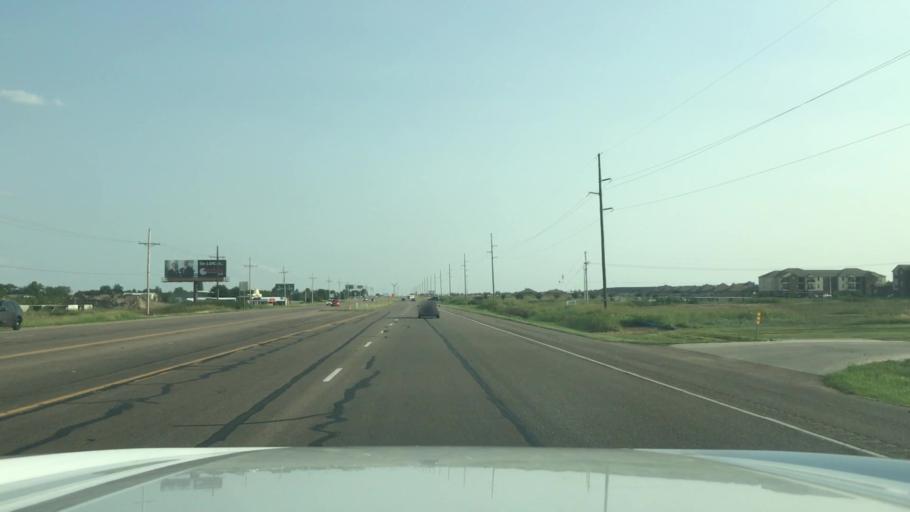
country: US
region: Texas
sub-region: Potter County
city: Amarillo
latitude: 35.1337
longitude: -101.9382
